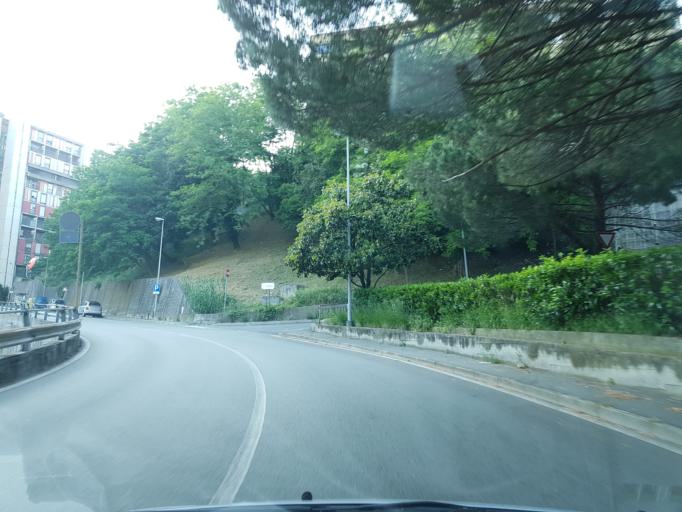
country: IT
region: Liguria
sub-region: Provincia di Genova
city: Genoa
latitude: 44.4524
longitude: 8.9071
